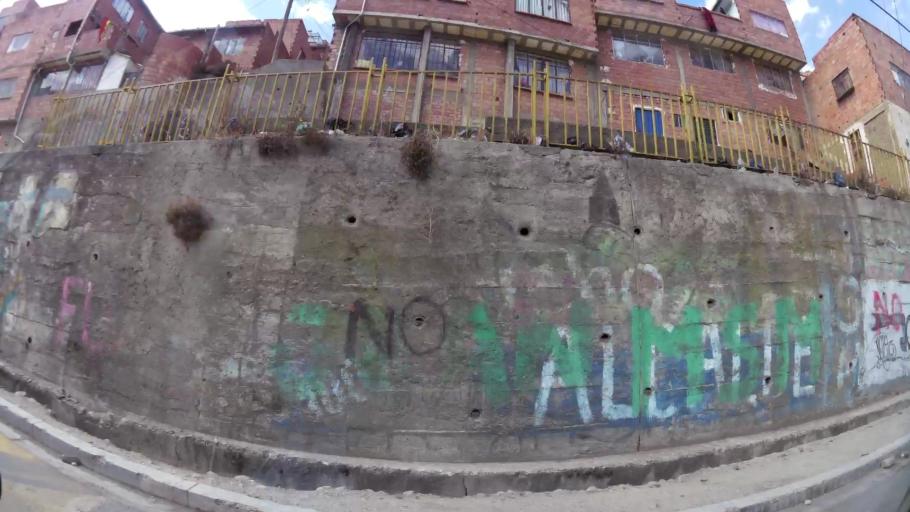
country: BO
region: La Paz
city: La Paz
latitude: -16.4648
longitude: -68.1173
